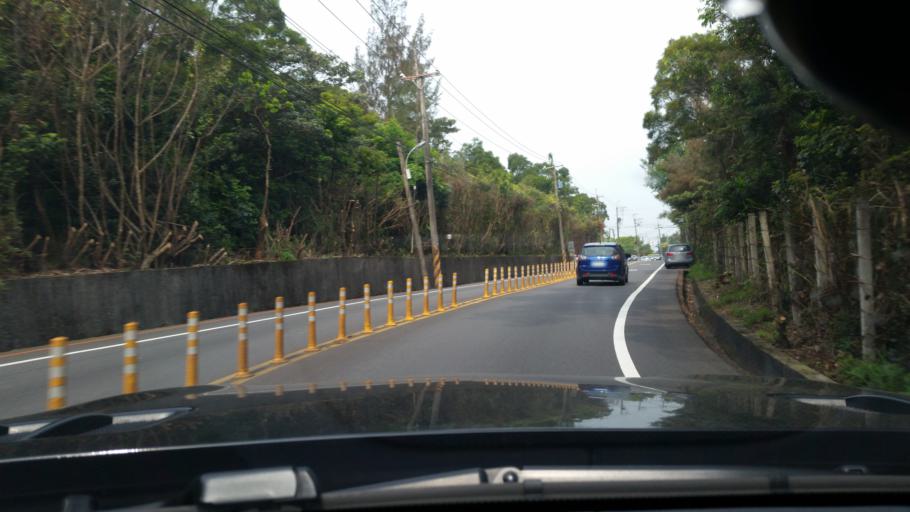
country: TW
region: Taiwan
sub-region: Taoyuan
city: Taoyuan
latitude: 25.0583
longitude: 121.3239
